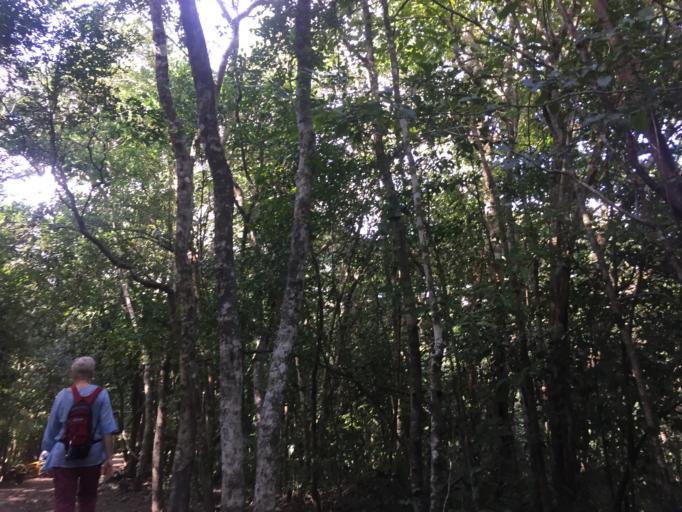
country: MX
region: Quintana Roo
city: Coba
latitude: 20.4846
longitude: -87.7231
